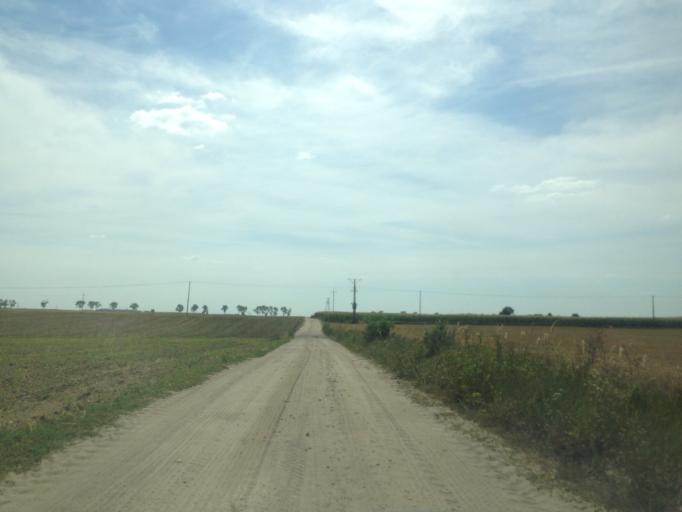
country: PL
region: Kujawsko-Pomorskie
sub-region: Powiat brodnicki
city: Gorzno
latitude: 53.2087
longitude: 19.6244
